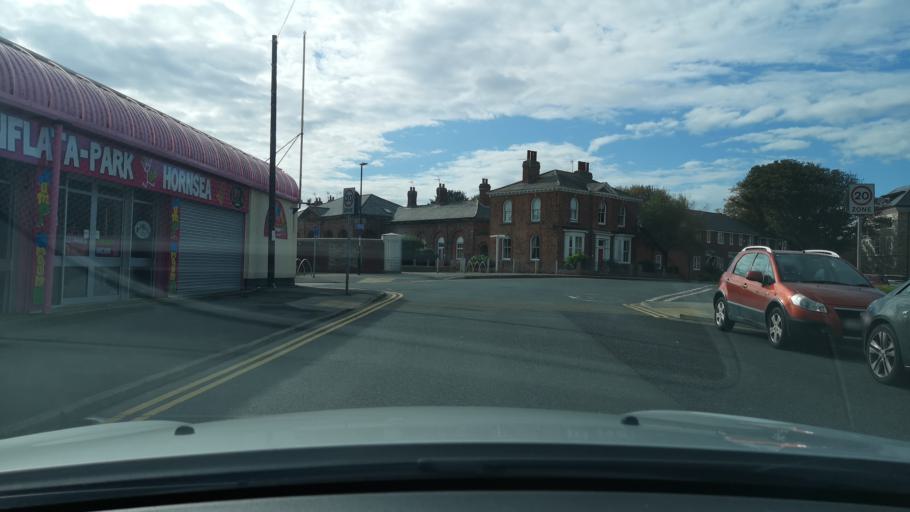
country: GB
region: England
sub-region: East Riding of Yorkshire
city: Hornsea
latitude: 53.9116
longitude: -0.1623
